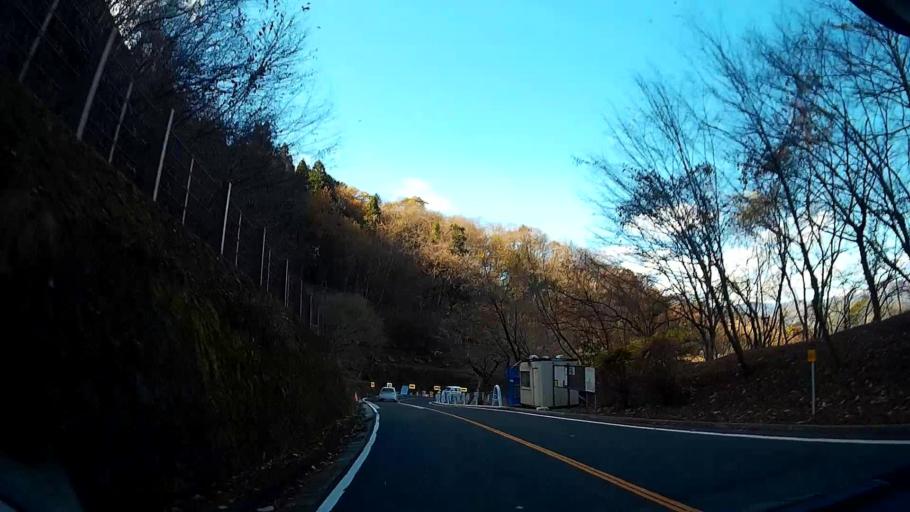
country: JP
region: Yamanashi
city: Uenohara
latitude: 35.7556
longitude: 139.0308
